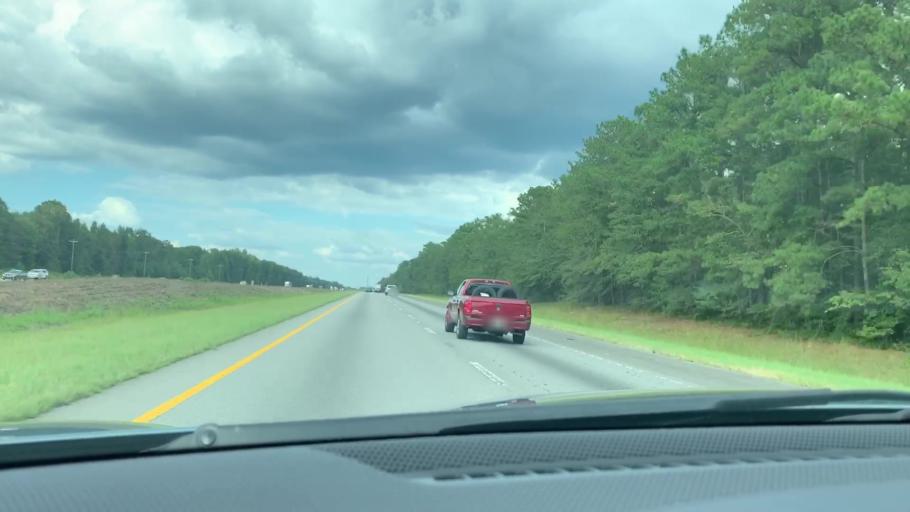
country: US
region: South Carolina
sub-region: Jasper County
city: Ridgeland
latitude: 32.5462
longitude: -80.9502
